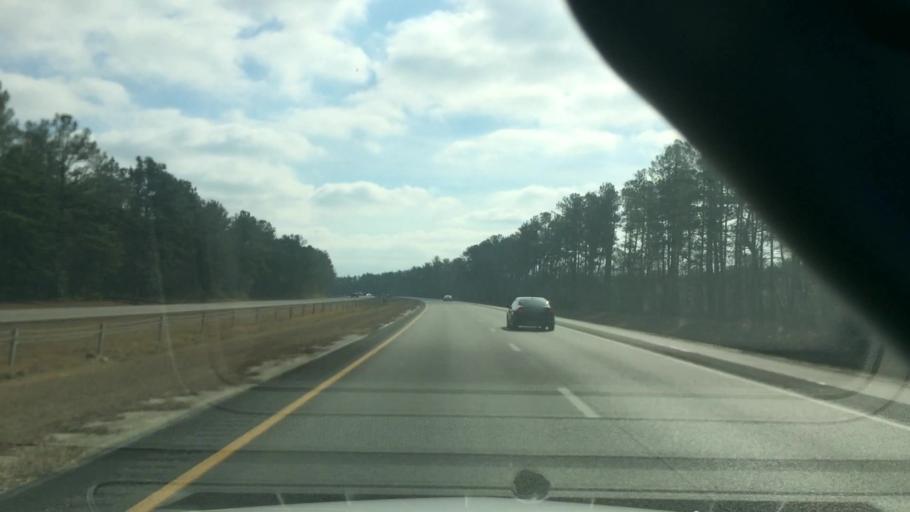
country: US
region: North Carolina
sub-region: Pender County
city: Burgaw
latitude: 34.5361
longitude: -77.8935
